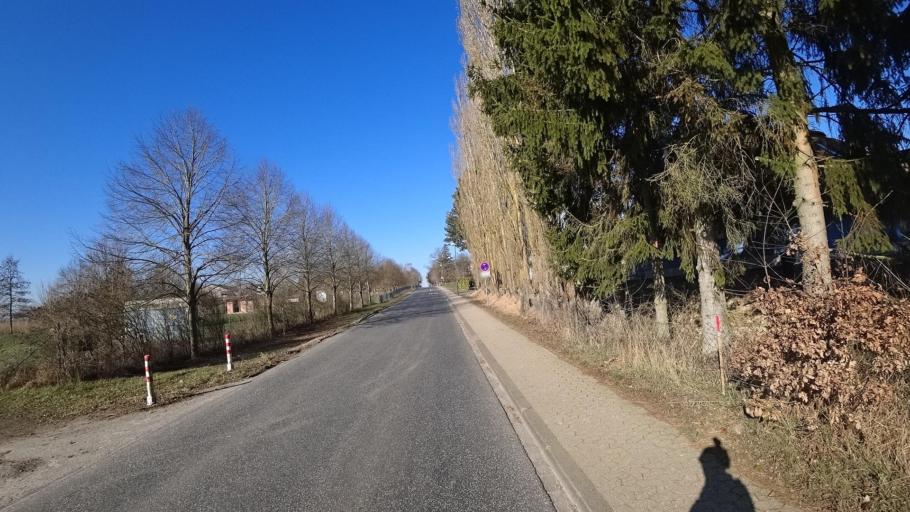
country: DE
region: Rheinland-Pfalz
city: Keidelheim
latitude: 49.9794
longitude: 7.5036
